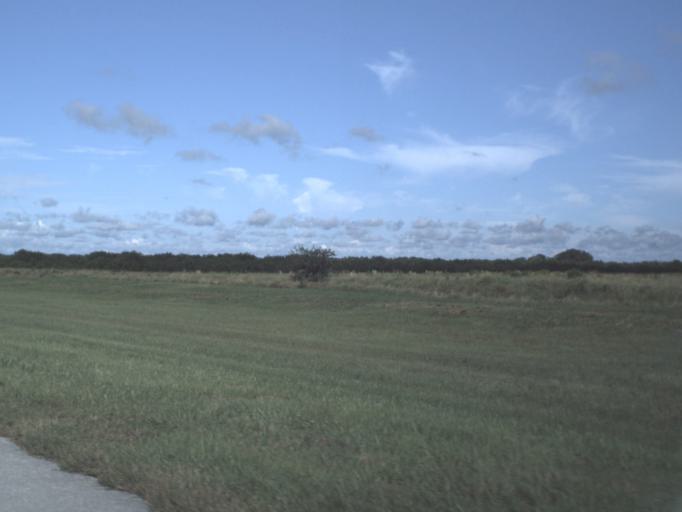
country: US
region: Florida
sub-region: Highlands County
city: Placid Lakes
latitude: 27.2097
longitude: -81.5892
